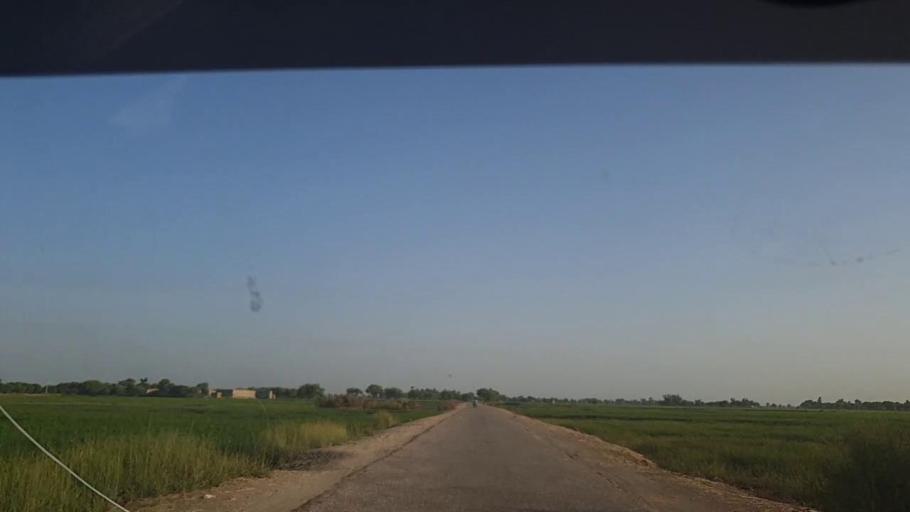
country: PK
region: Sindh
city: Thul
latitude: 28.2134
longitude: 68.8696
